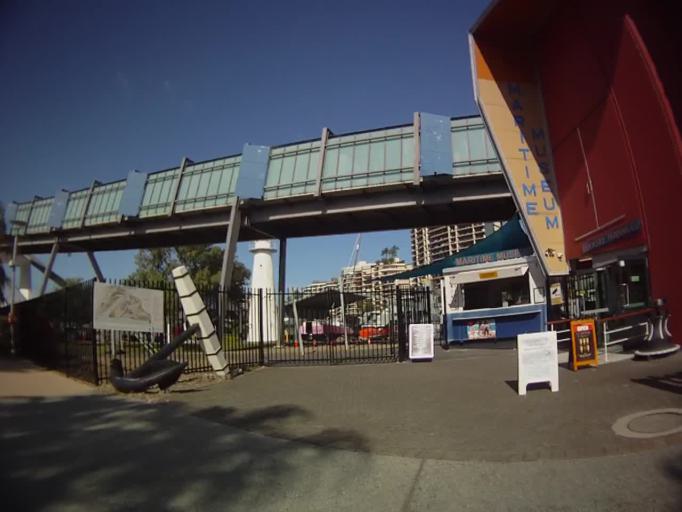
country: AU
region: Queensland
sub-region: Brisbane
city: South Brisbane
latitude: -27.4814
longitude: 153.0260
